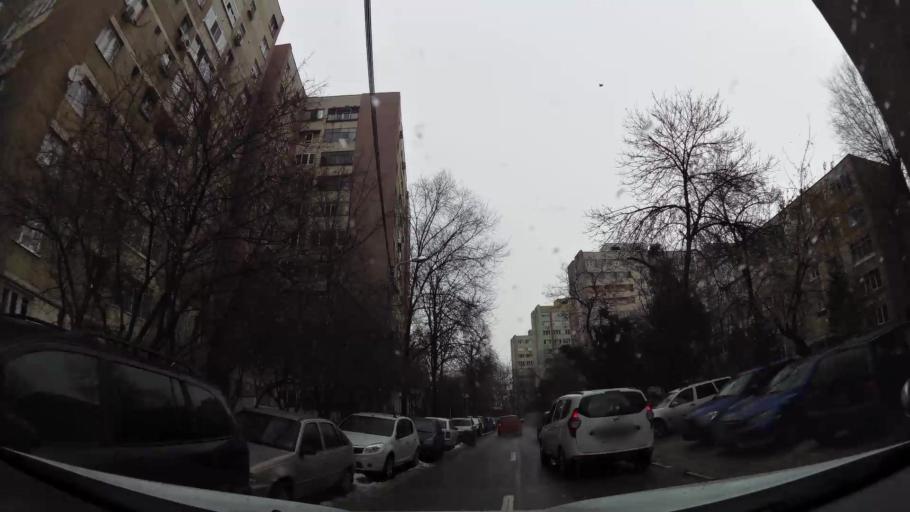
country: RO
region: Ilfov
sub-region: Comuna Chiajna
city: Rosu
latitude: 44.4187
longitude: 26.0245
